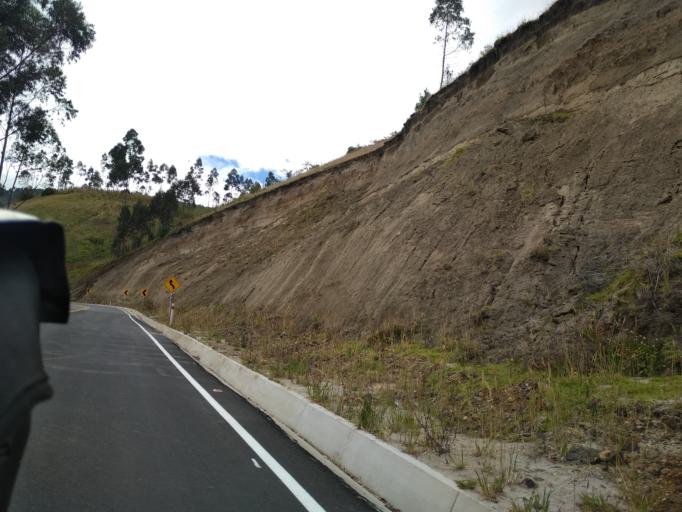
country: EC
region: Cotopaxi
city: Saquisili
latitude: -0.7520
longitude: -78.9029
